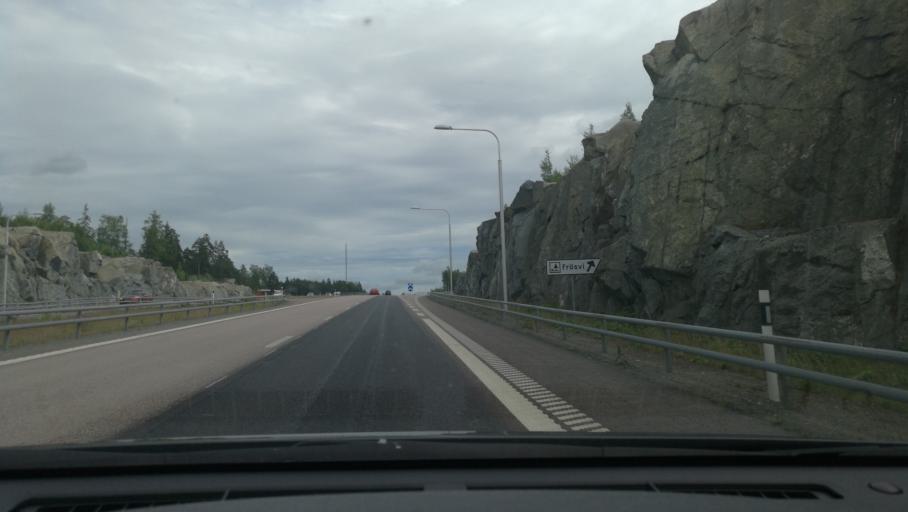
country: SE
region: Uppsala
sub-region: Enkopings Kommun
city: Hummelsta
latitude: 59.6381
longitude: 16.8766
